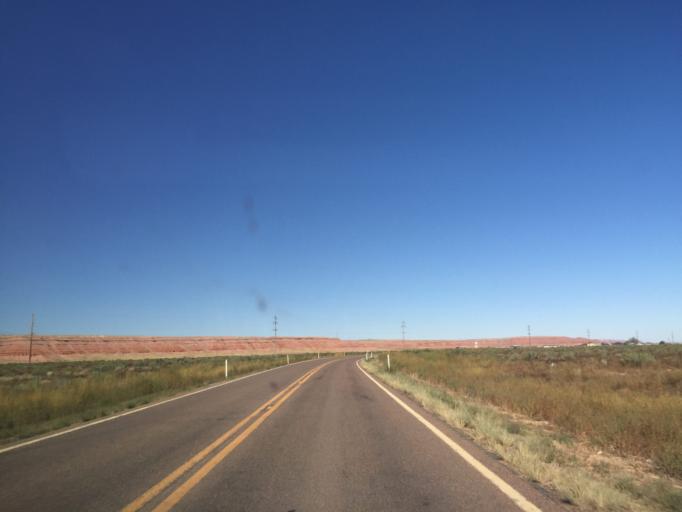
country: US
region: Arizona
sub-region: Apache County
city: Many Farms
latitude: 36.3335
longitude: -109.6235
